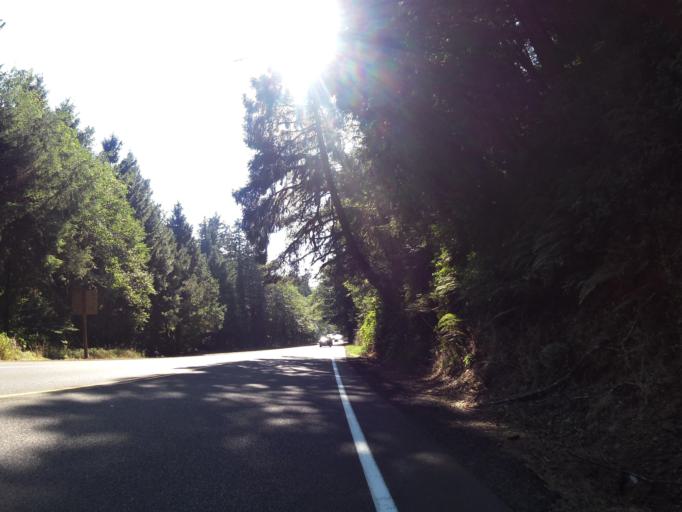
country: US
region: Oregon
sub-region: Clatsop County
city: Cannon Beach
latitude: 45.7643
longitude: -123.9536
